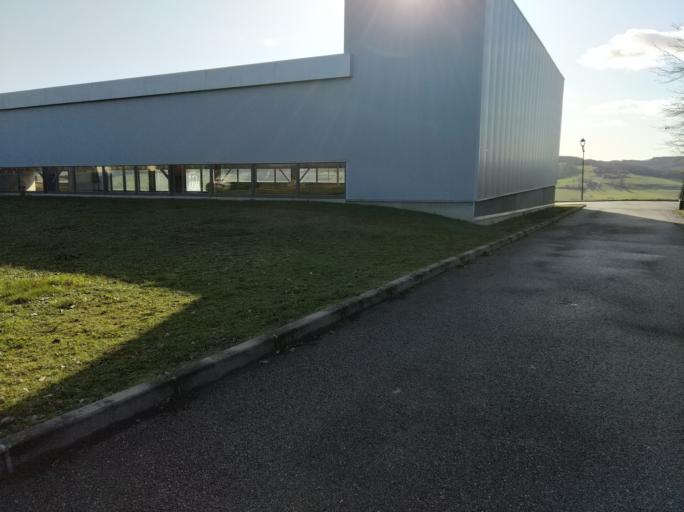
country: FR
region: Rhone-Alpes
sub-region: Departement de la Drome
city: Hauterives
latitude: 45.2702
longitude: 5.0964
